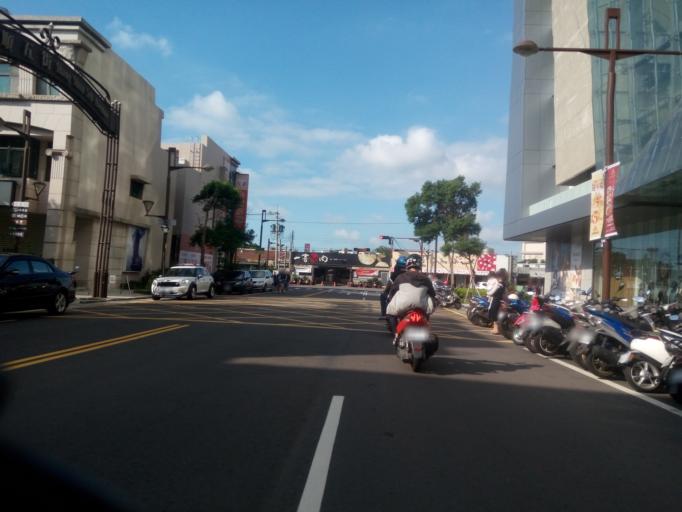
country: TW
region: Taiwan
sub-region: Hsinchu
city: Hsinchu
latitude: 24.6888
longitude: 120.9035
